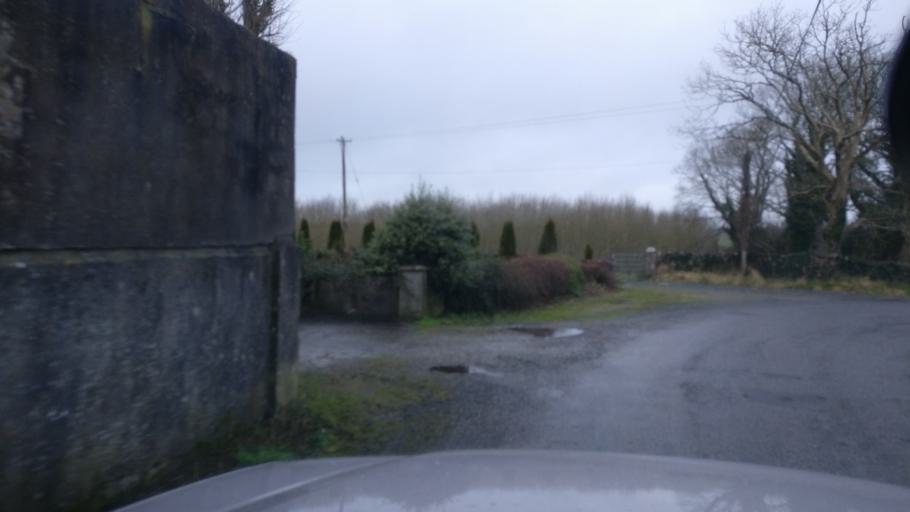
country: IE
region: Connaught
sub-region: County Galway
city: Loughrea
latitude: 53.1752
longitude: -8.6126
